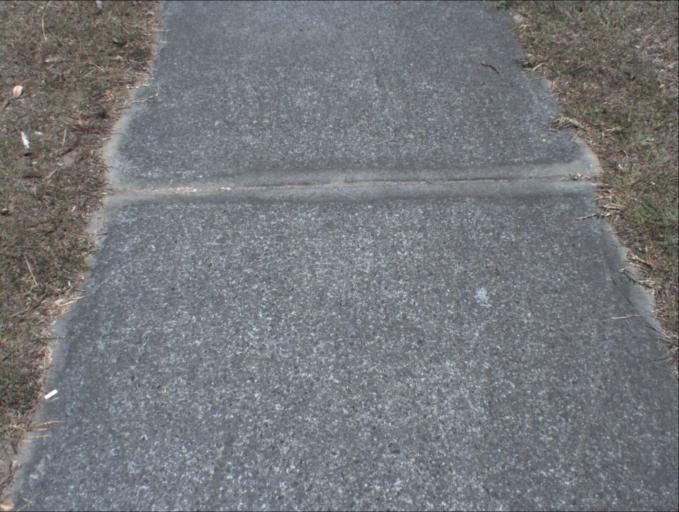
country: AU
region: Queensland
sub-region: Logan
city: Beenleigh
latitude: -27.7021
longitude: 153.2095
